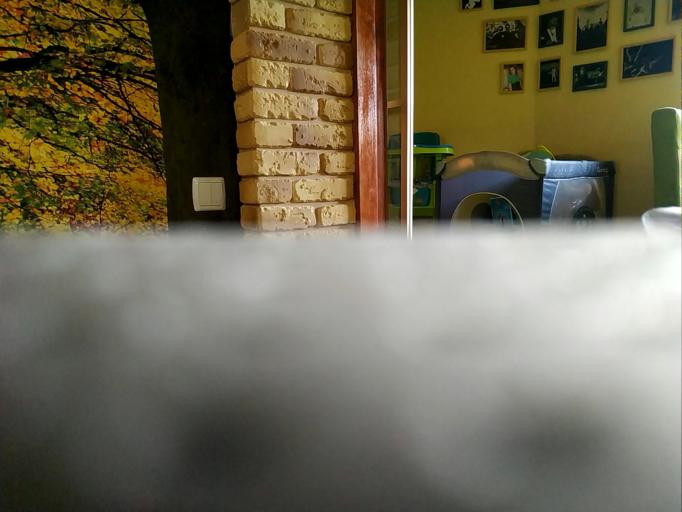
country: RU
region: Kaluga
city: Sukhinichi
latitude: 54.0574
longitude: 35.2957
